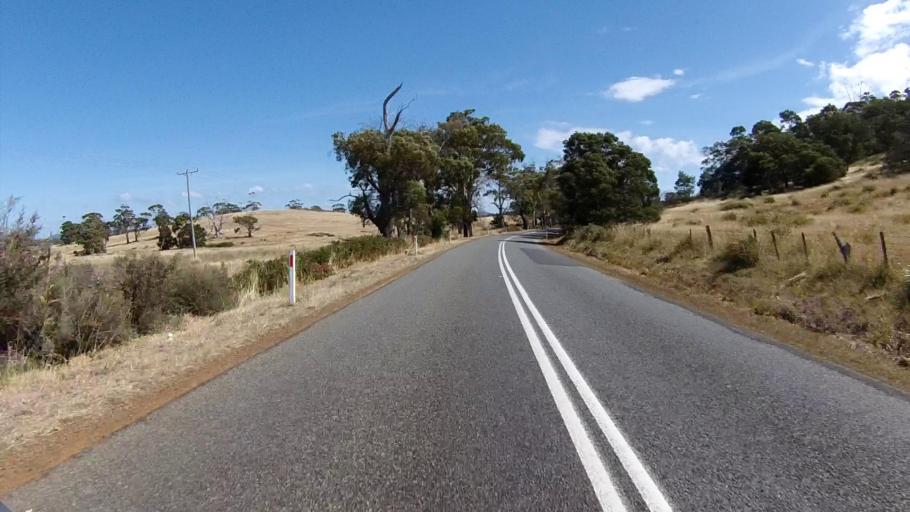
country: AU
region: Tasmania
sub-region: Sorell
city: Sorell
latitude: -42.3006
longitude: 147.9795
